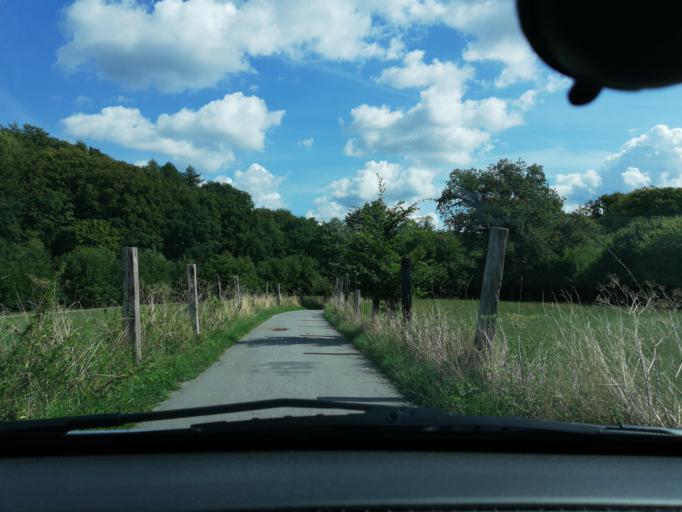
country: DE
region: North Rhine-Westphalia
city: Wetter (Ruhr)
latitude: 51.3771
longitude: 7.3524
